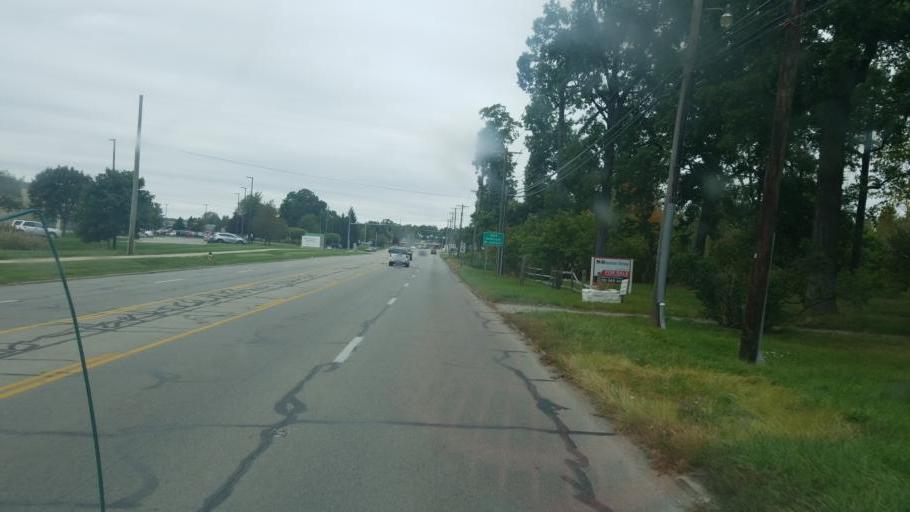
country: US
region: Ohio
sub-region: Lucas County
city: Ottawa Hills
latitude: 41.6736
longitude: -83.6697
